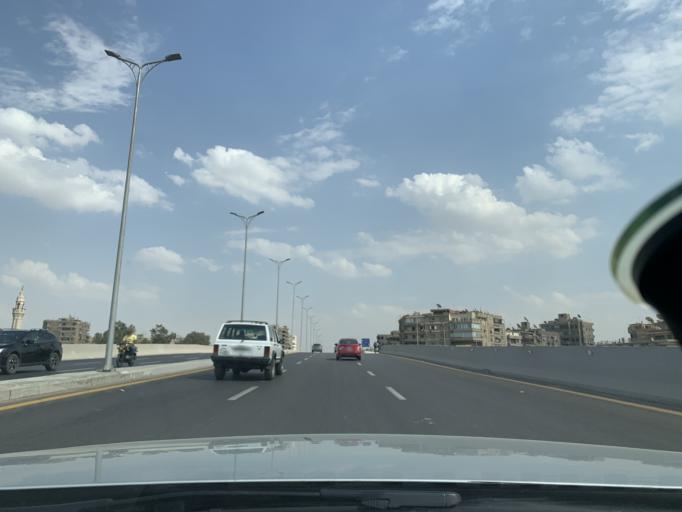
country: EG
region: Muhafazat al Qalyubiyah
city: Al Khankah
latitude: 30.1124
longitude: 31.3451
